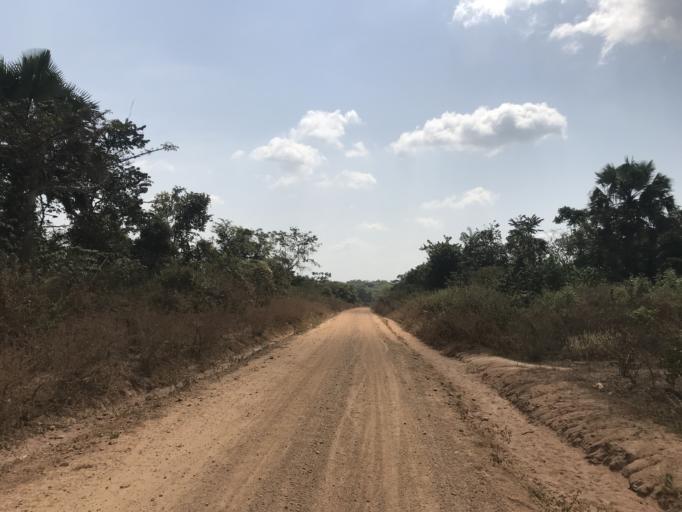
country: NG
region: Osun
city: Ifon
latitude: 7.9325
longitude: 4.4834
